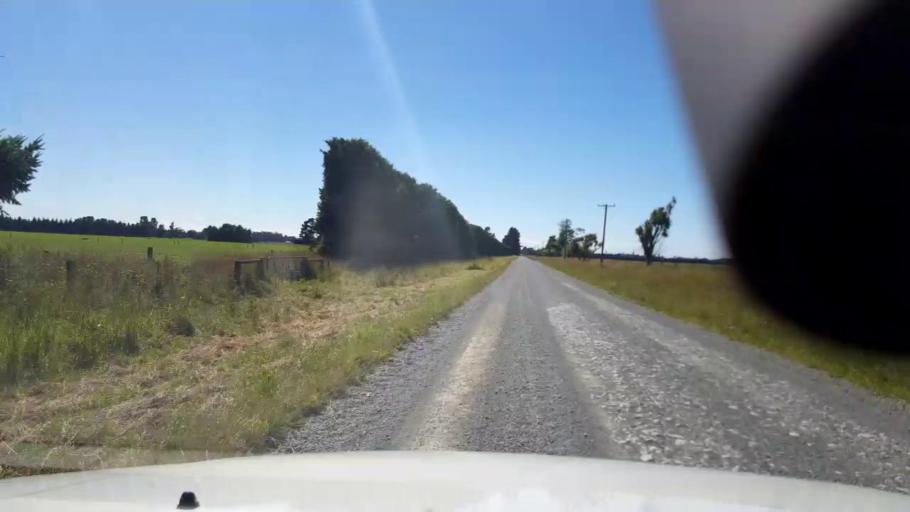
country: NZ
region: Canterbury
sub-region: Timaru District
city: Pleasant Point
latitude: -43.9708
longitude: 171.2408
